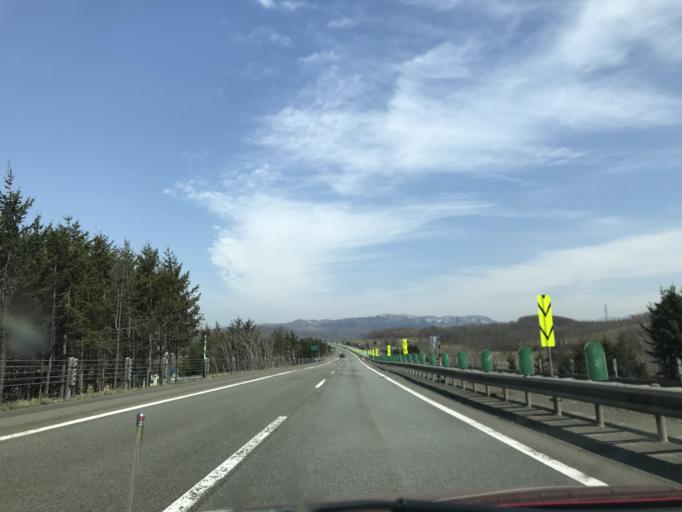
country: JP
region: Hokkaido
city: Iwamizawa
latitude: 43.2160
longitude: 141.8229
